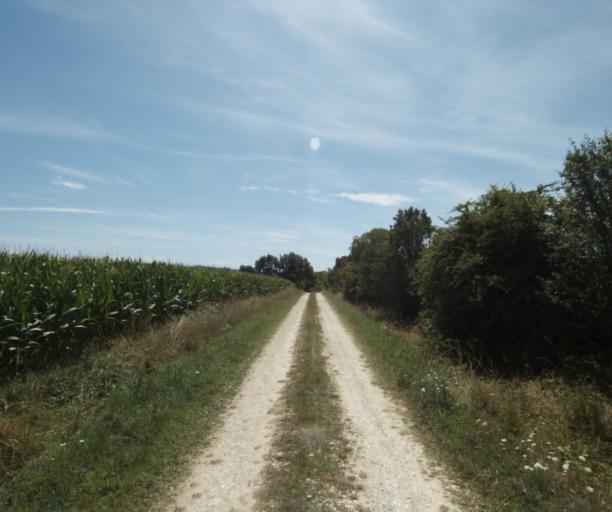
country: FR
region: Midi-Pyrenees
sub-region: Departement de la Haute-Garonne
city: Revel
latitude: 43.5023
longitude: 2.0159
